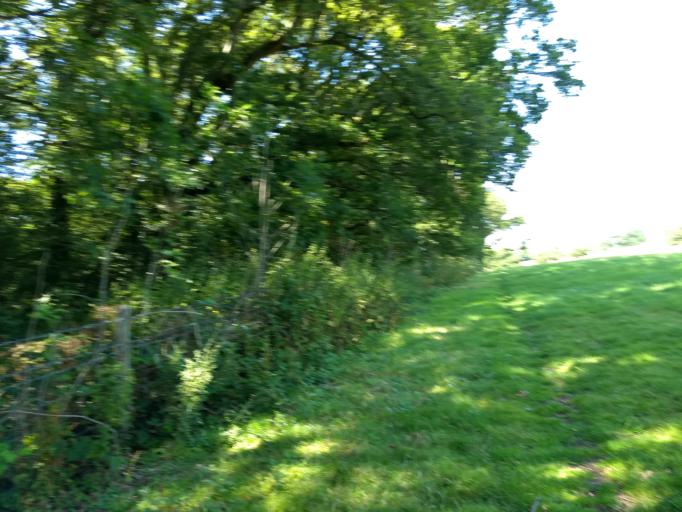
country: GB
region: England
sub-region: Isle of Wight
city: Brading
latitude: 50.7008
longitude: -1.1589
